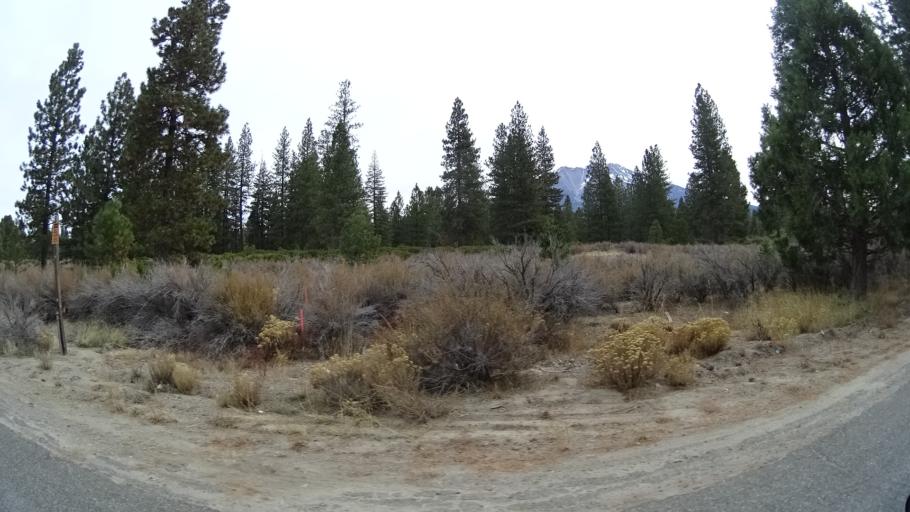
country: US
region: California
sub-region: Siskiyou County
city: Weed
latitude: 41.3950
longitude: -122.3739
